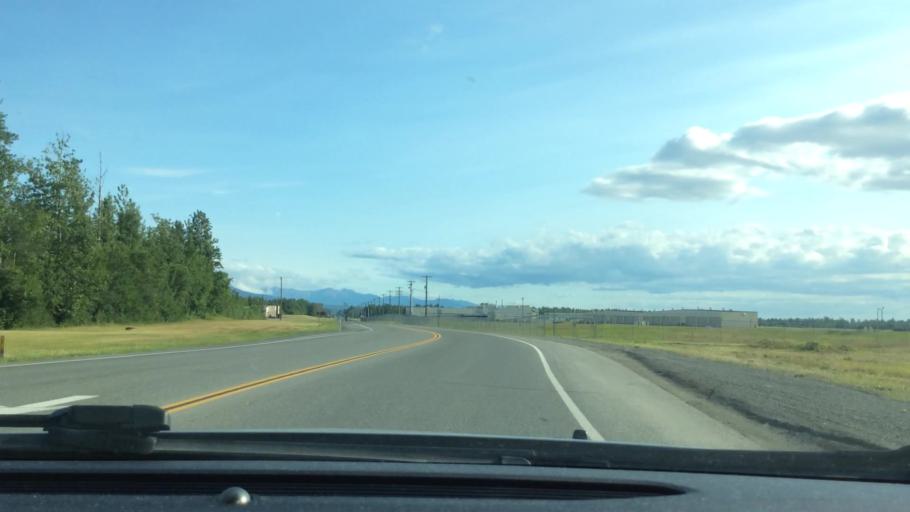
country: US
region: Alaska
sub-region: Anchorage Municipality
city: Anchorage
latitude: 61.2521
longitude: -149.7784
